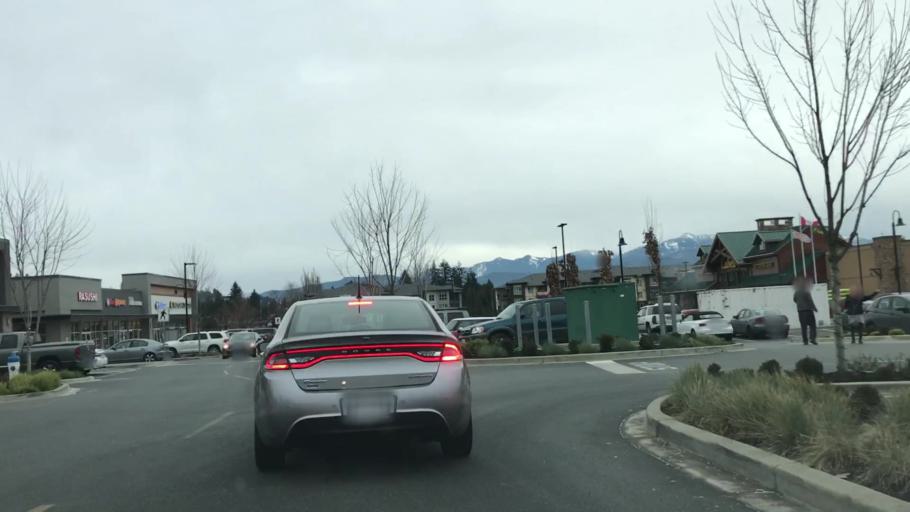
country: CA
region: British Columbia
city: Abbotsford
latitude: 49.0363
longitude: -122.2917
